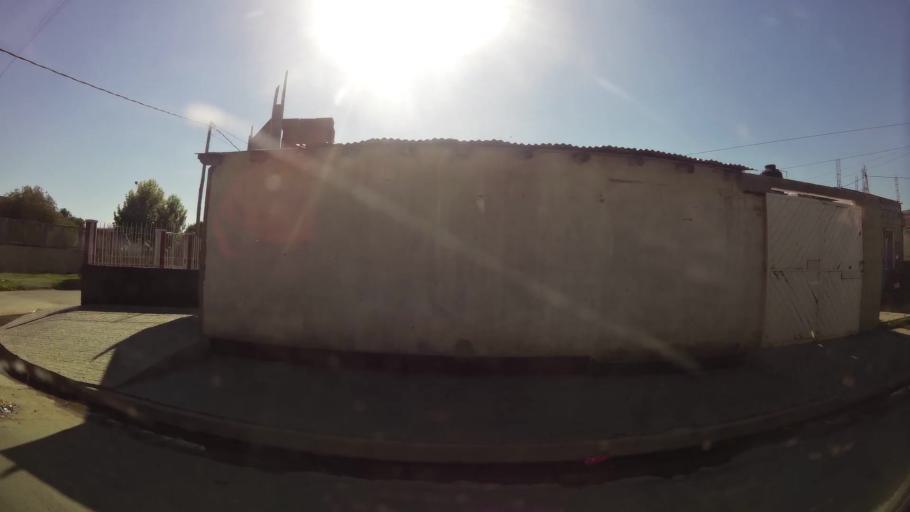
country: AR
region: Cordoba
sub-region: Departamento de Capital
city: Cordoba
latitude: -31.3714
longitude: -64.1934
